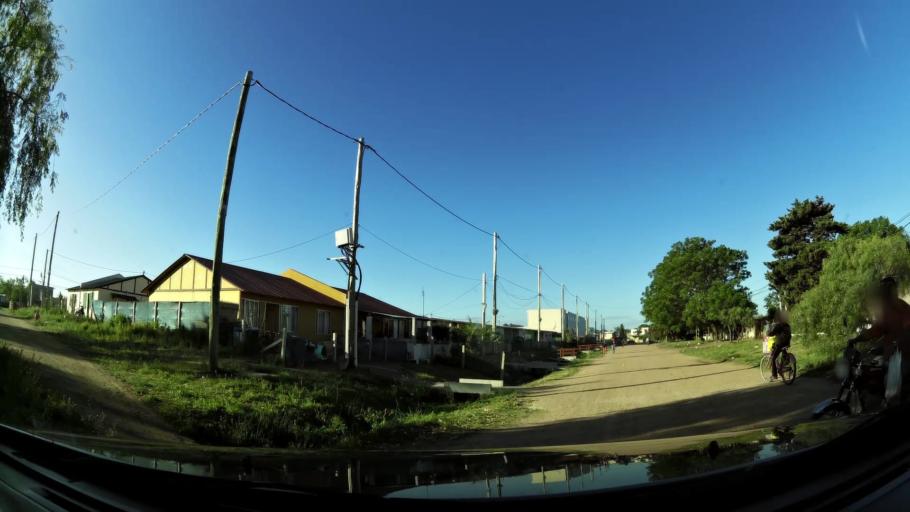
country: UY
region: Canelones
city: Paso de Carrasco
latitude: -34.8545
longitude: -56.0533
